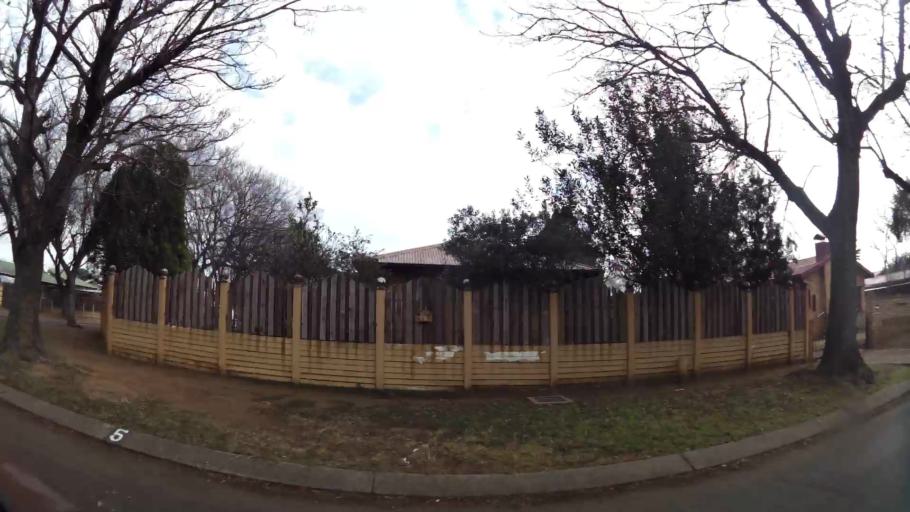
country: ZA
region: Gauteng
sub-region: Sedibeng District Municipality
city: Vanderbijlpark
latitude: -26.6835
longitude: 27.8144
